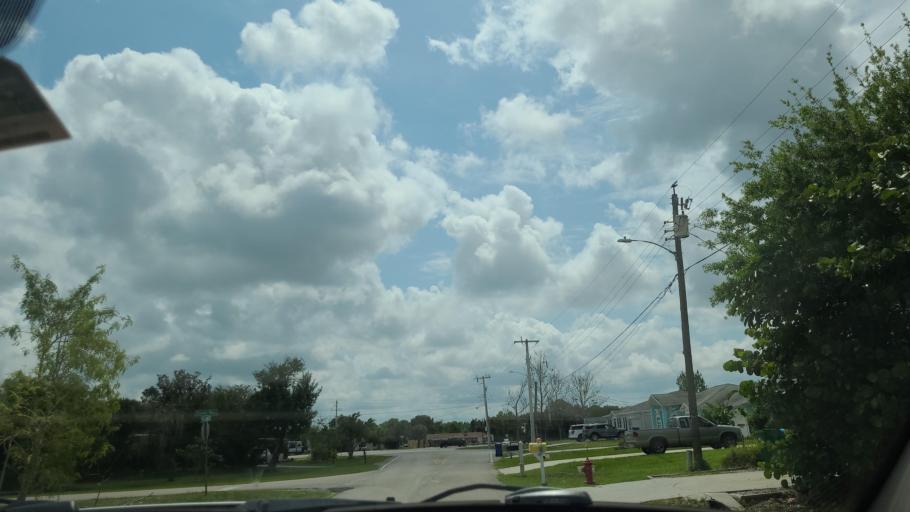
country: US
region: Florida
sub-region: Indian River County
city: Sebastian
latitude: 27.7963
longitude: -80.4837
